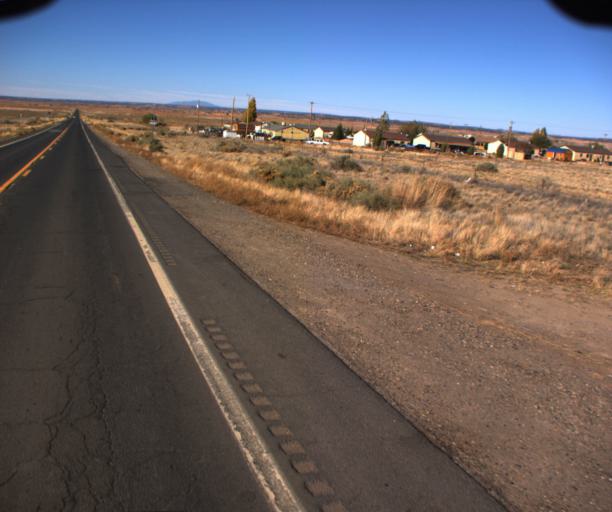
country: US
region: Arizona
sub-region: Coconino County
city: Kaibito
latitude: 36.4622
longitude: -110.6927
